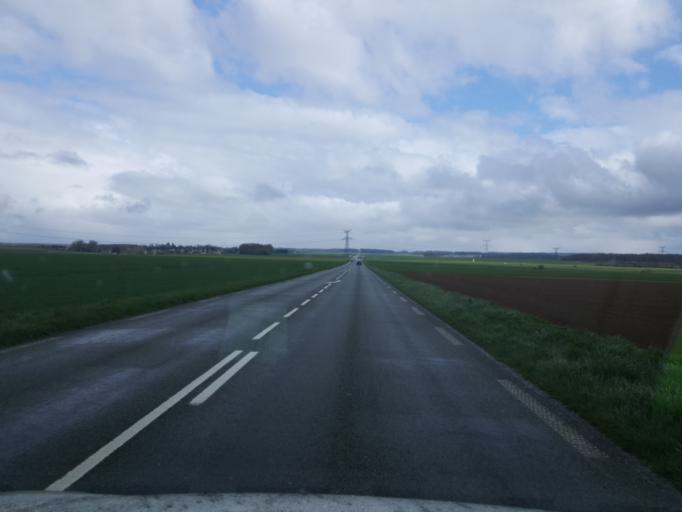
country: FR
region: Picardie
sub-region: Departement de l'Oise
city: Chaumont-en-Vexin
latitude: 49.3109
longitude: 1.8771
